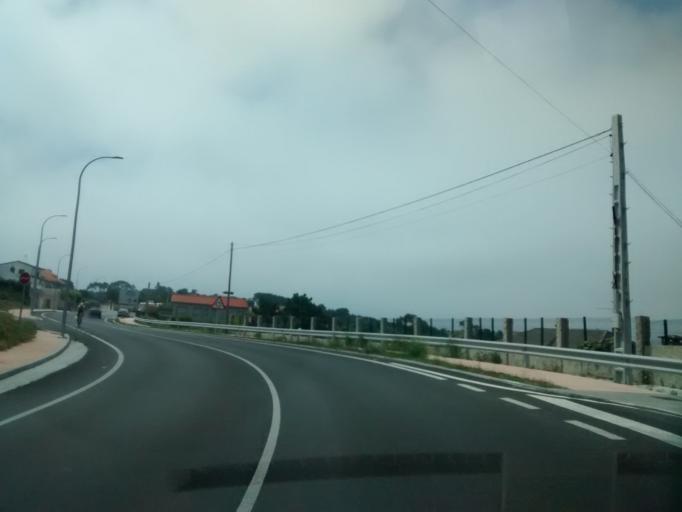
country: ES
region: Galicia
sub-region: Provincia de Pontevedra
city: O Grove
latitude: 42.4242
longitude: -8.8743
